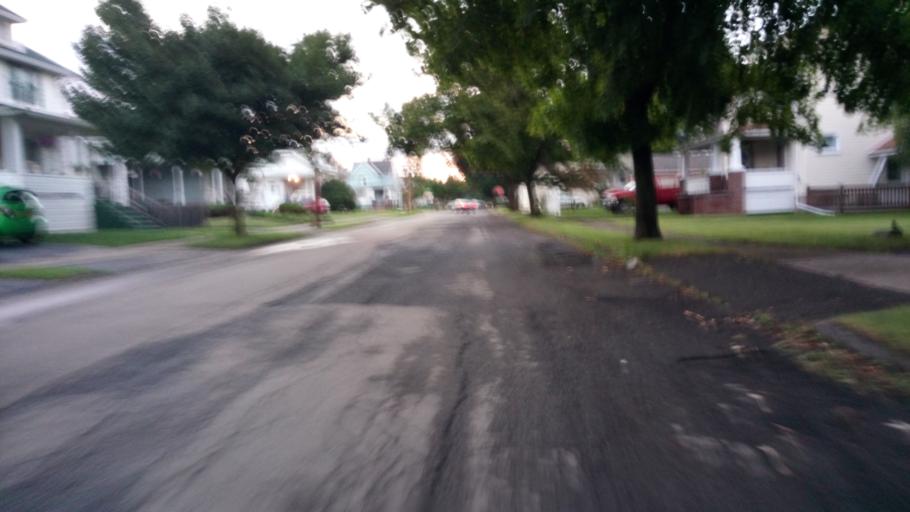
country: US
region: New York
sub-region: Chemung County
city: Elmira
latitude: 42.0997
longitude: -76.8217
